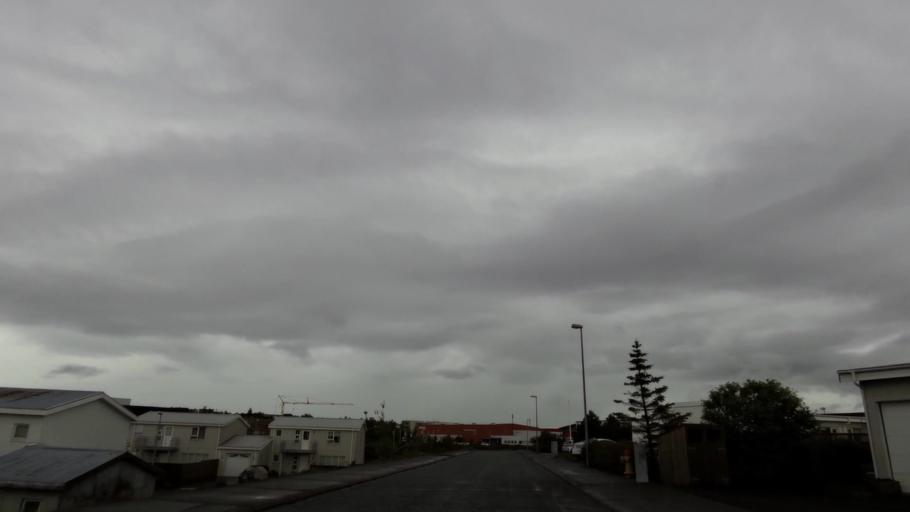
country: IS
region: Capital Region
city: Hafnarfjoerdur
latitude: 64.0503
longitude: -21.9747
